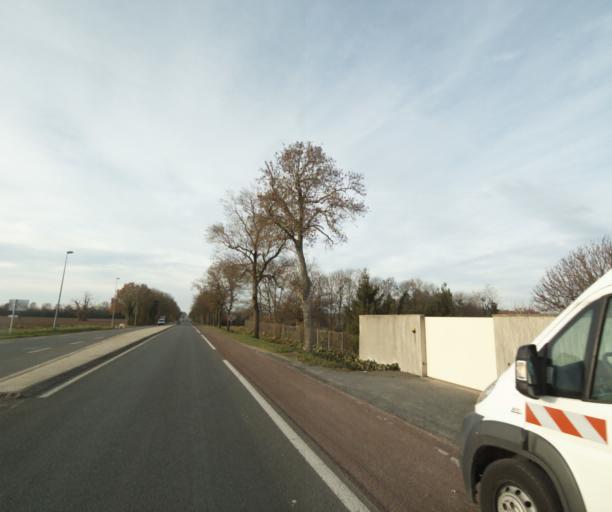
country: FR
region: Poitou-Charentes
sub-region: Departement de la Charente-Maritime
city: Saint-Georges-des-Coteaux
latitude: 45.7784
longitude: -0.7018
